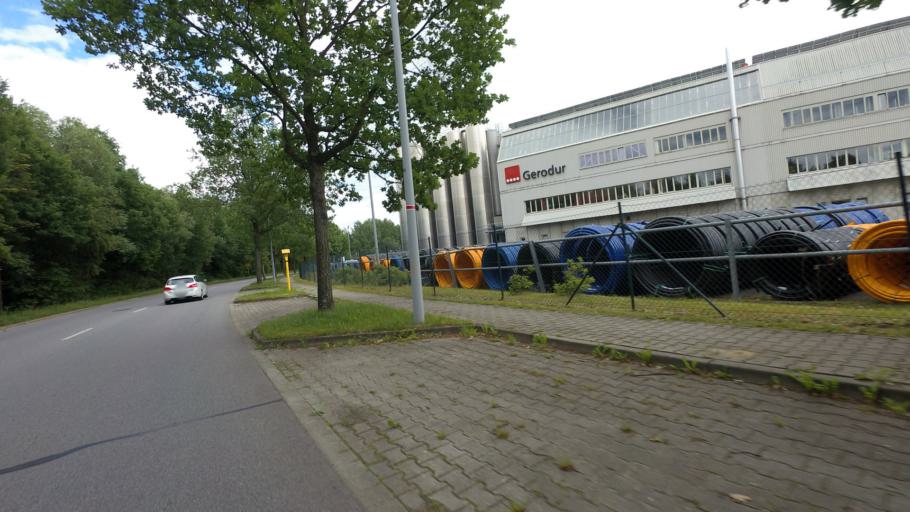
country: DE
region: Saxony
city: Neustadt in Sachsen
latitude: 51.0362
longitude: 14.2246
